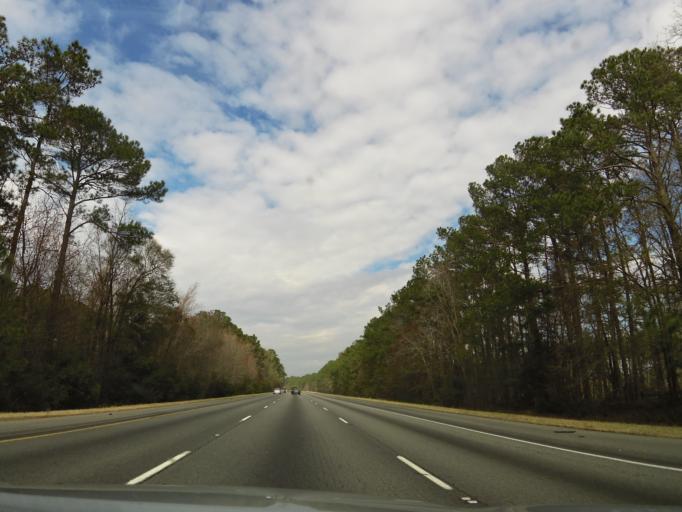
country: US
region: Georgia
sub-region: Bryan County
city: Richmond Hill
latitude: 31.8638
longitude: -81.3363
